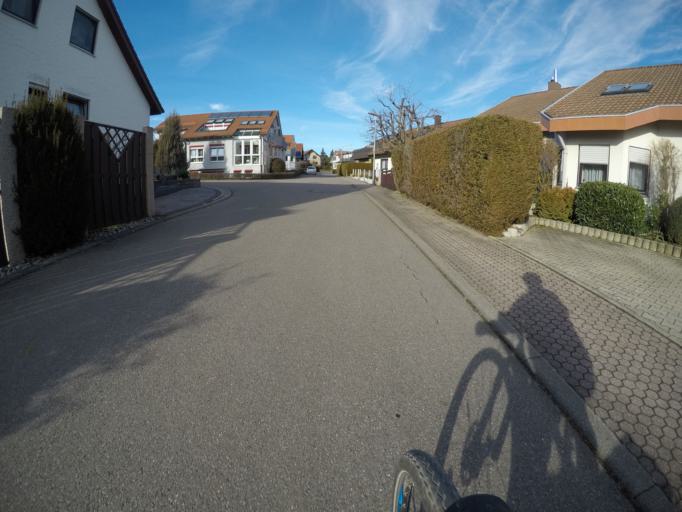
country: DE
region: Baden-Wuerttemberg
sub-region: Regierungsbezirk Stuttgart
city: Nufringen
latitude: 48.6227
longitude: 8.8813
